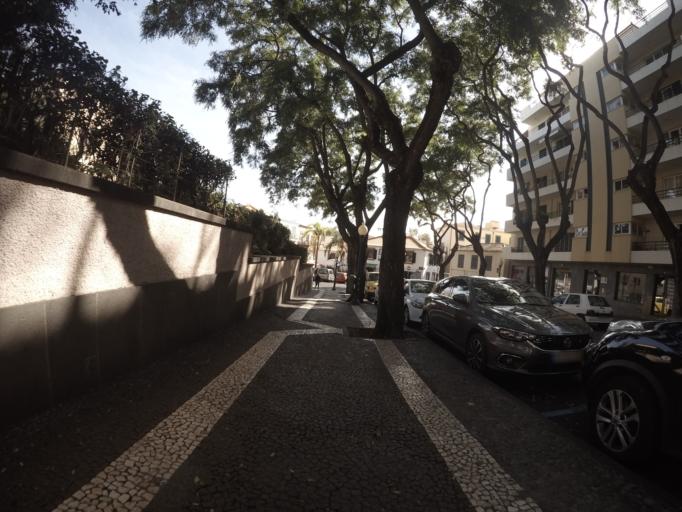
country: PT
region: Madeira
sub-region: Funchal
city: Funchal
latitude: 32.6490
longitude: -16.9021
